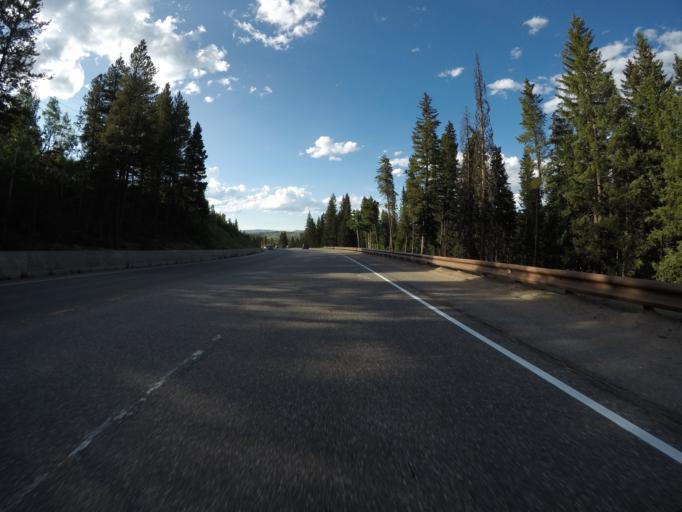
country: US
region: Colorado
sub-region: Grand County
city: Fraser
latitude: 39.9063
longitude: -105.7805
